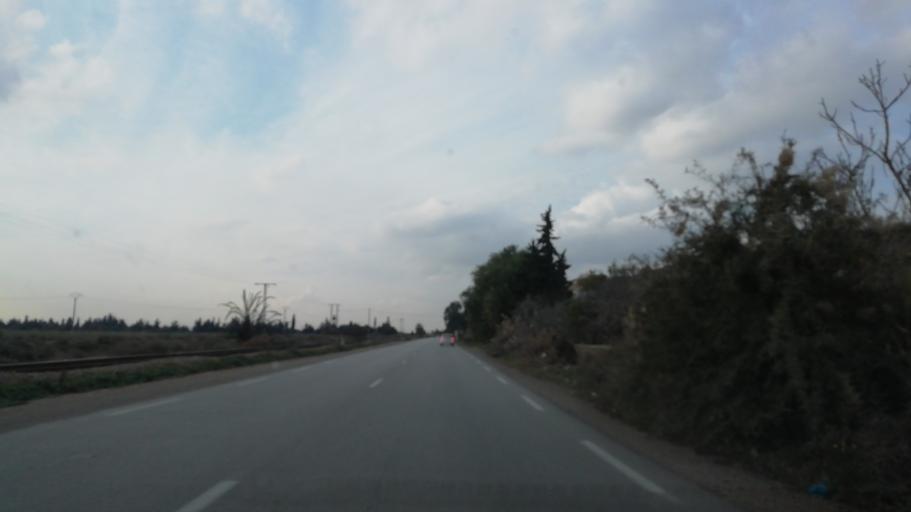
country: DZ
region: Mascara
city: Sig
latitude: 35.6620
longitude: 0.0066
